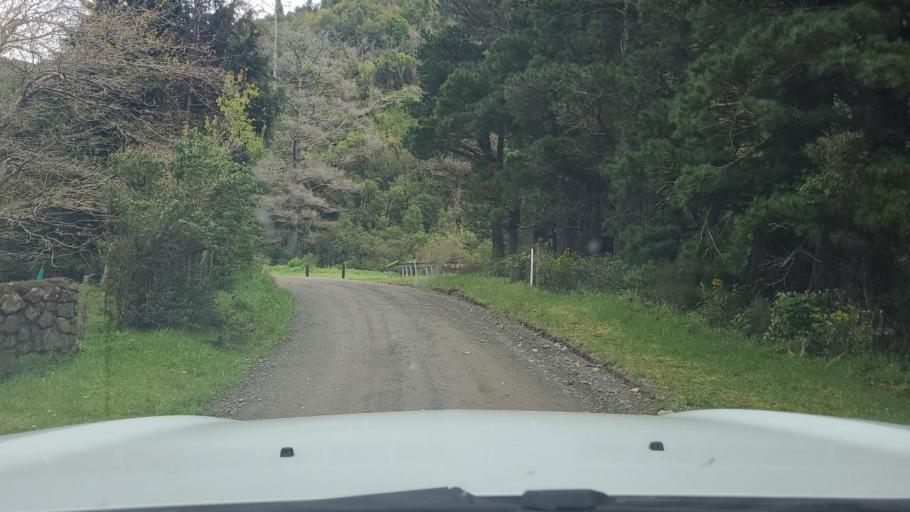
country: NZ
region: Wellington
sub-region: Masterton District
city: Masterton
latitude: -40.9380
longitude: 175.4656
